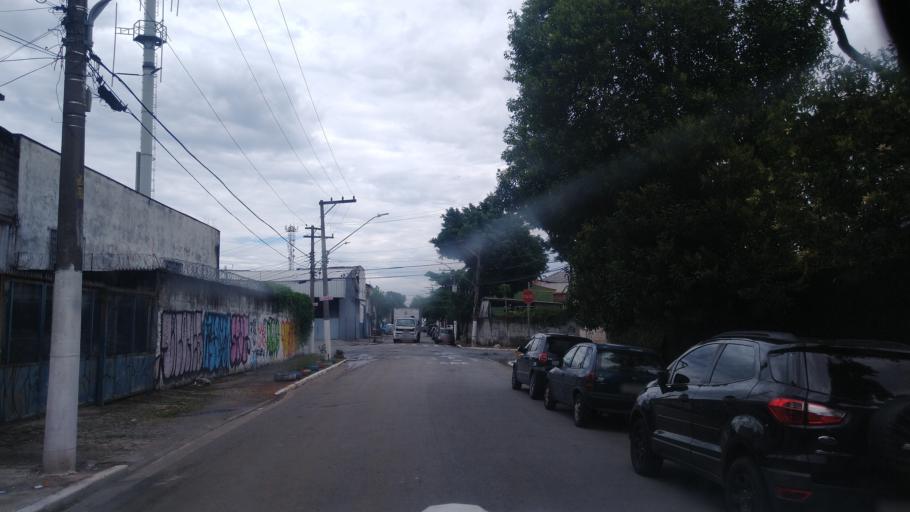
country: BR
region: Sao Paulo
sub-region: Guarulhos
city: Guarulhos
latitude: -23.5216
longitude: -46.5649
